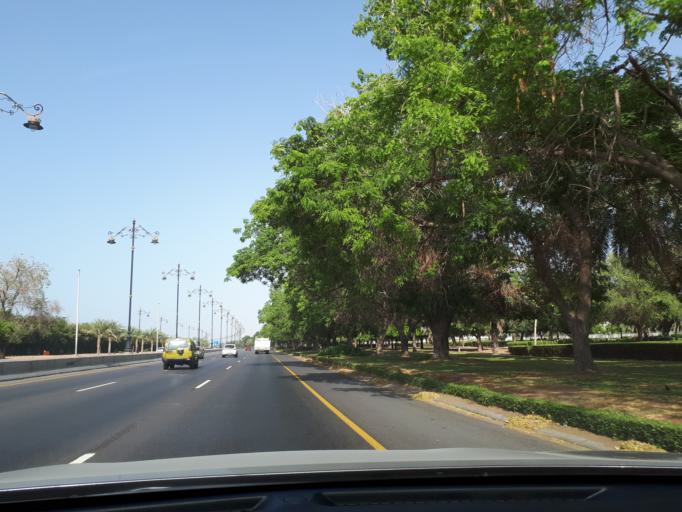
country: OM
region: Muhafazat Masqat
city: Bawshar
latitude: 23.5890
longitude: 58.3141
